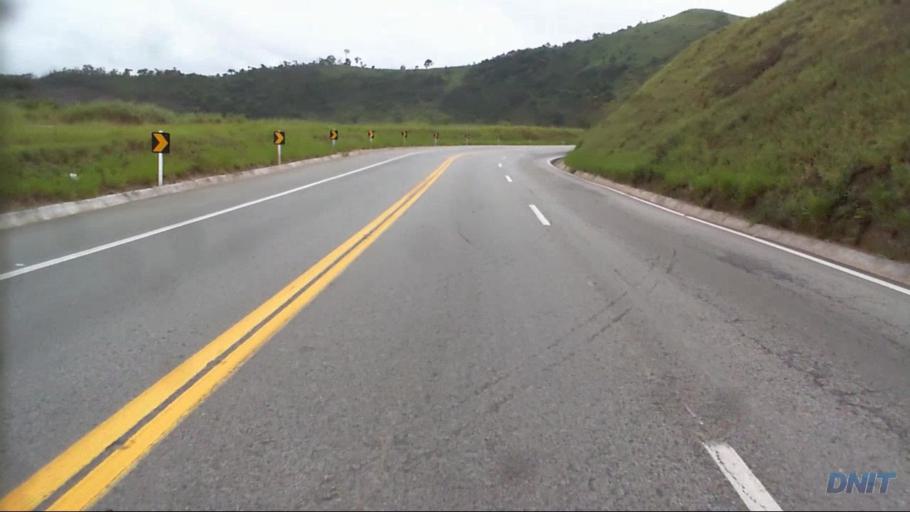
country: BR
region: Minas Gerais
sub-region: Nova Era
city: Nova Era
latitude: -19.6334
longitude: -42.8926
